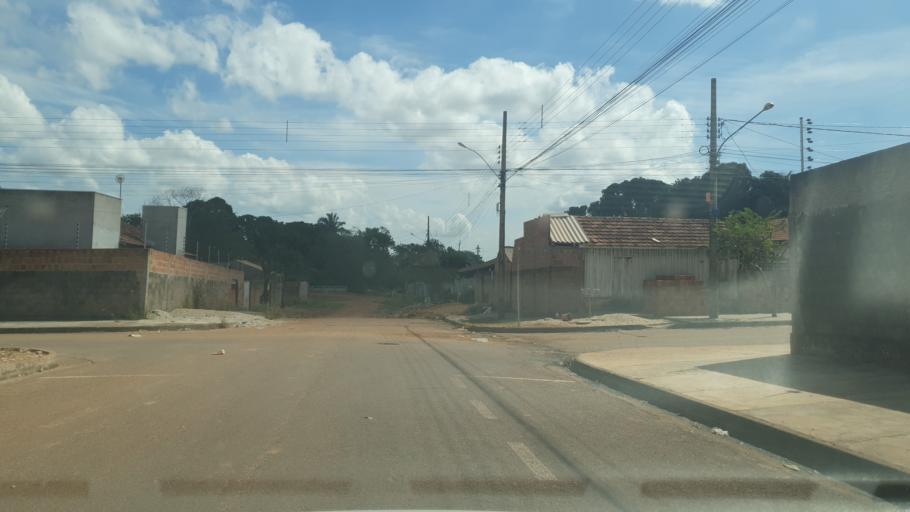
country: BR
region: Mato Grosso
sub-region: Pontes E Lacerda
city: Pontes e Lacerda
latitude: -15.2263
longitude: -59.3436
